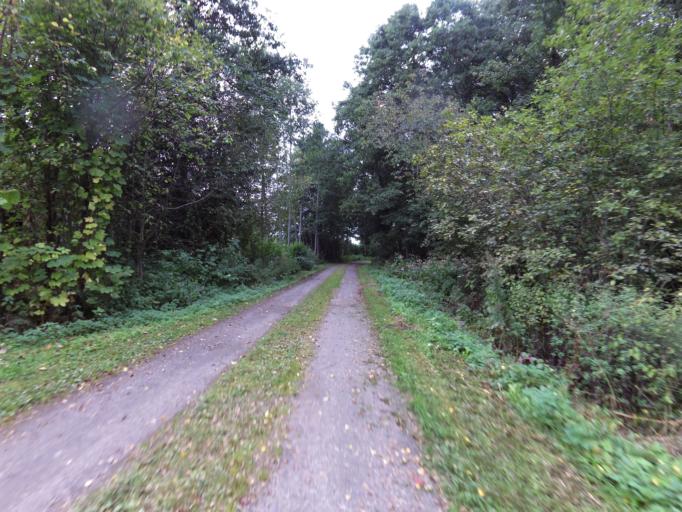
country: SE
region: Gaevleborg
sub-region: Gavle Kommun
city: Valbo
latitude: 60.7541
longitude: 16.9726
